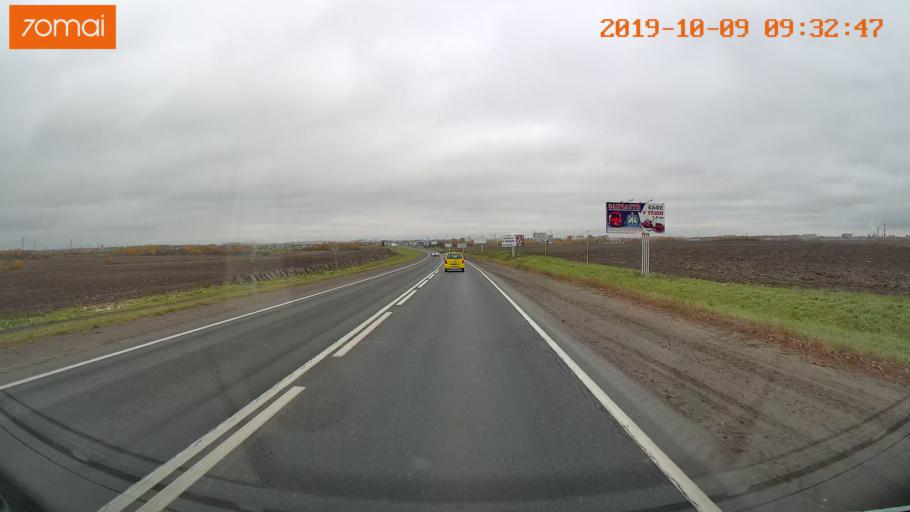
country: RU
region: Vologda
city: Vologda
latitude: 59.1623
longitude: 39.9239
